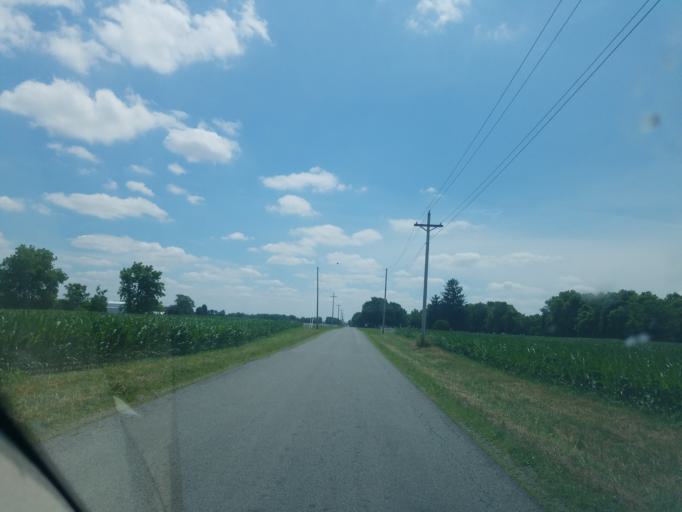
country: US
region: Ohio
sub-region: Wyandot County
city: Carey
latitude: 40.9515
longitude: -83.5134
